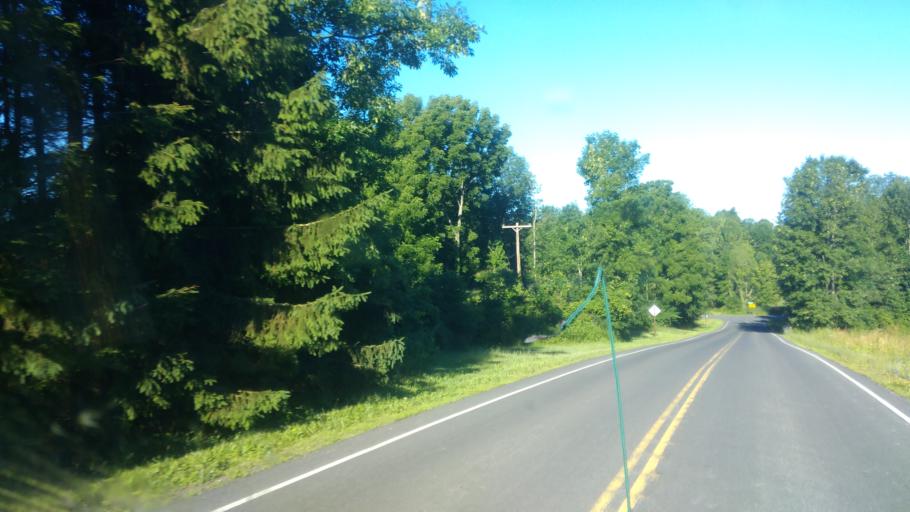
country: US
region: New York
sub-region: Wayne County
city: Sodus
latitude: 43.1506
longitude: -77.0462
